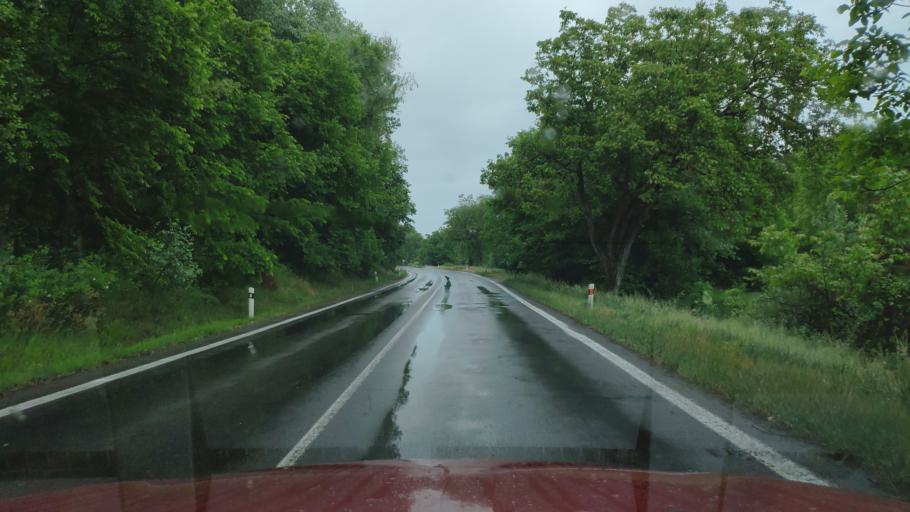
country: HU
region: Borsod-Abauj-Zemplen
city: Karcsa
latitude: 48.3913
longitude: 21.7715
